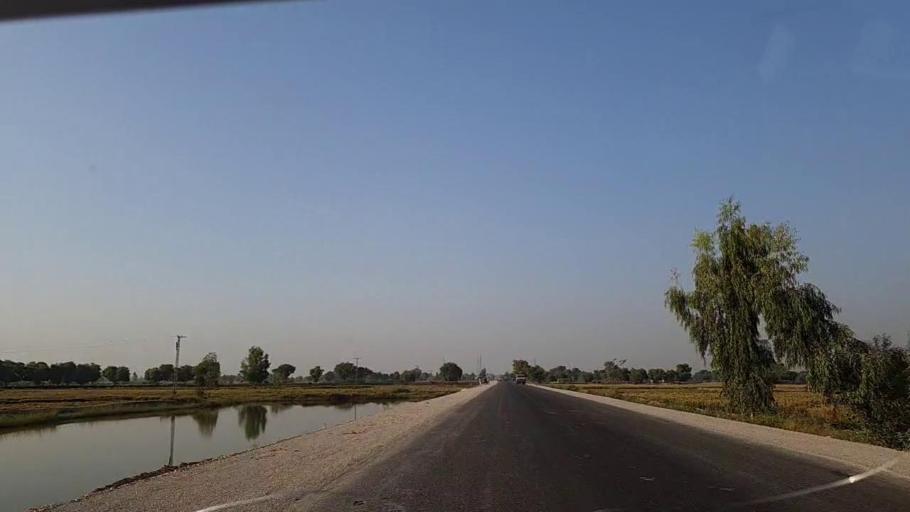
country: PK
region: Sindh
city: Rustam jo Goth
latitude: 27.9525
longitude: 68.8087
